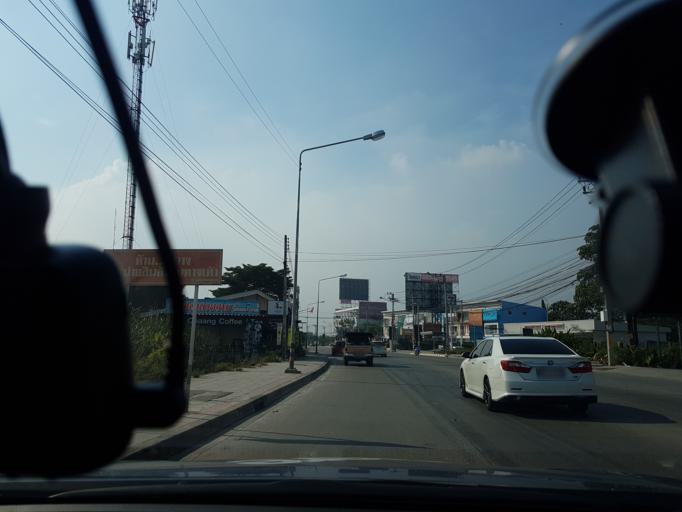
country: TH
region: Pathum Thani
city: Lam Luk Ka
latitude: 13.9216
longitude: 100.7108
